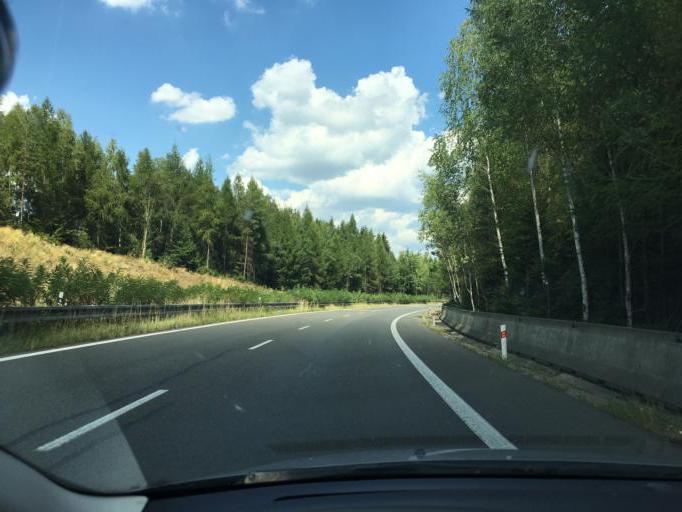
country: CZ
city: Hradek nad Nisou
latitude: 50.8121
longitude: 14.8984
